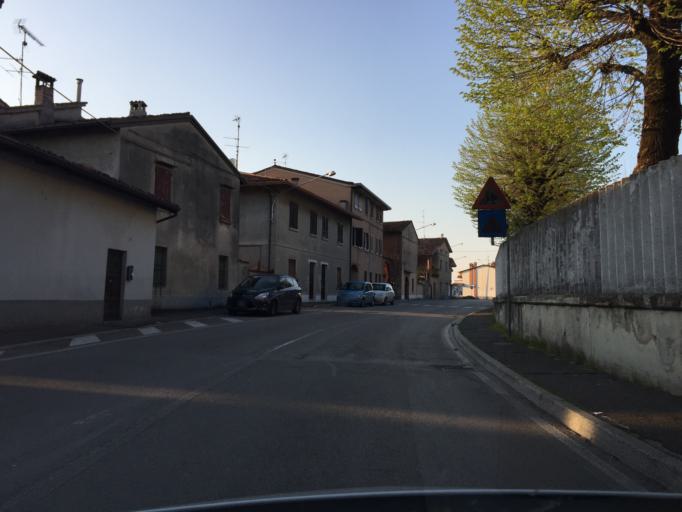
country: IT
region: Lombardy
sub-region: Provincia di Brescia
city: Pralboino
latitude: 45.2687
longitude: 10.2201
